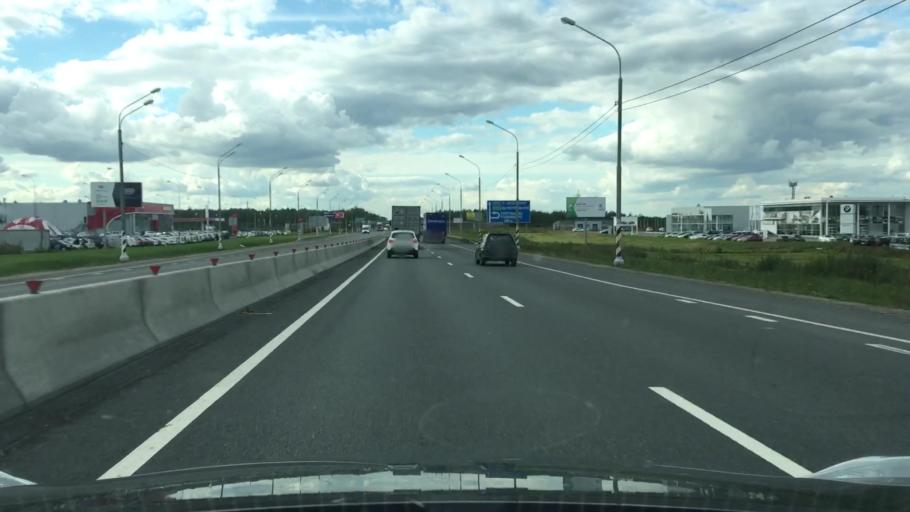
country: RU
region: Tverskaya
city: Tver
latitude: 56.7893
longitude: 35.9107
